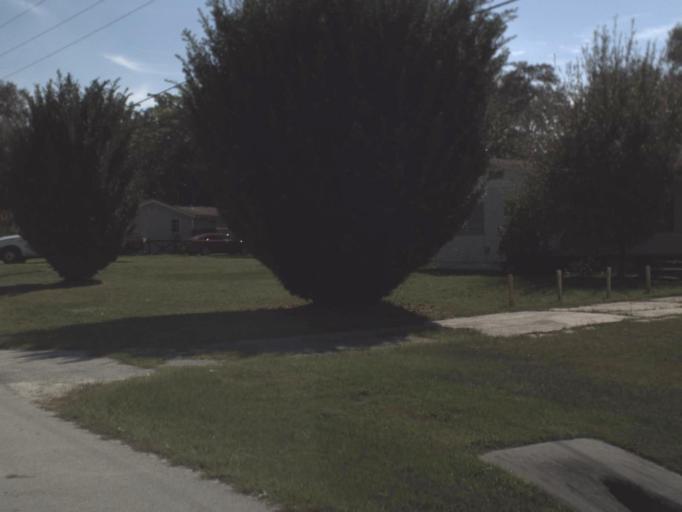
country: US
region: Florida
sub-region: Highlands County
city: Avon Park
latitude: 27.5956
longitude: -81.5184
